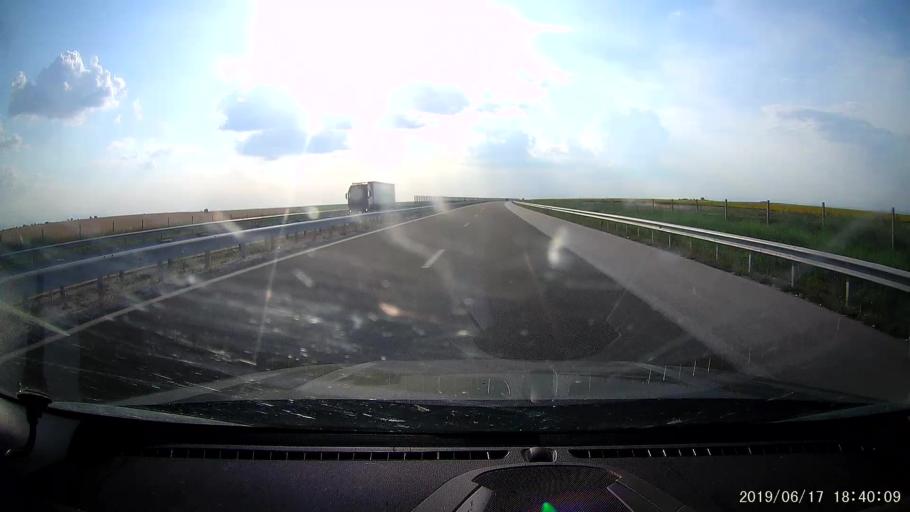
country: BG
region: Stara Zagora
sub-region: Obshtina Chirpan
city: Chirpan
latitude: 42.1521
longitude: 25.2861
